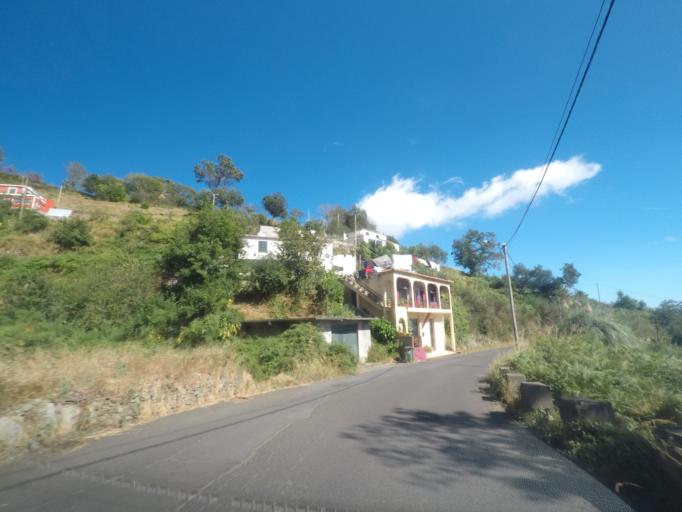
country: PT
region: Madeira
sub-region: Ribeira Brava
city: Campanario
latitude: 32.6971
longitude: -17.0180
